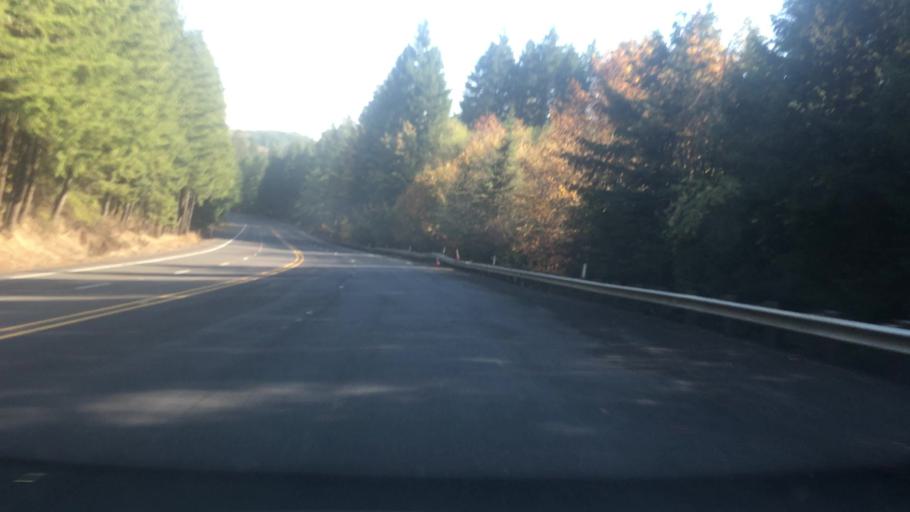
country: US
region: Oregon
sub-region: Polk County
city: Grand Ronde
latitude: 45.0585
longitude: -123.6855
